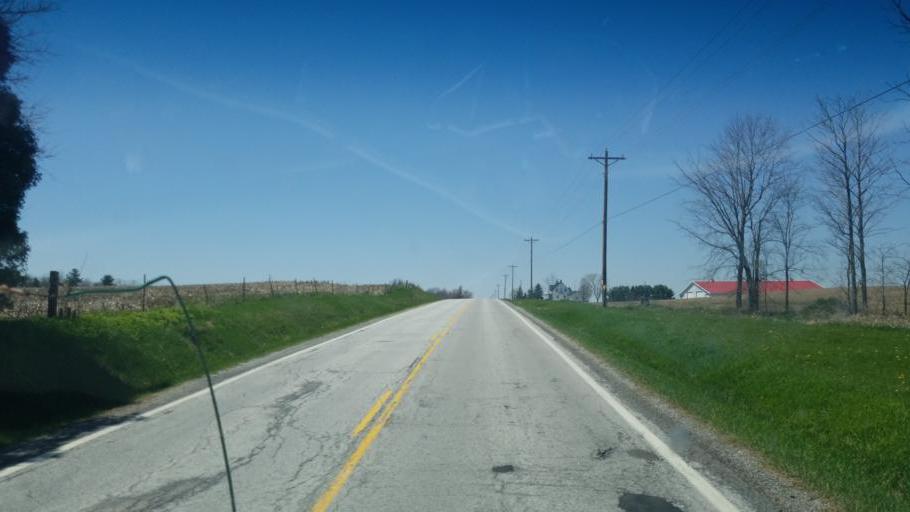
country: US
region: Ohio
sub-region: Huron County
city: New London
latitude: 41.0885
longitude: -82.4429
